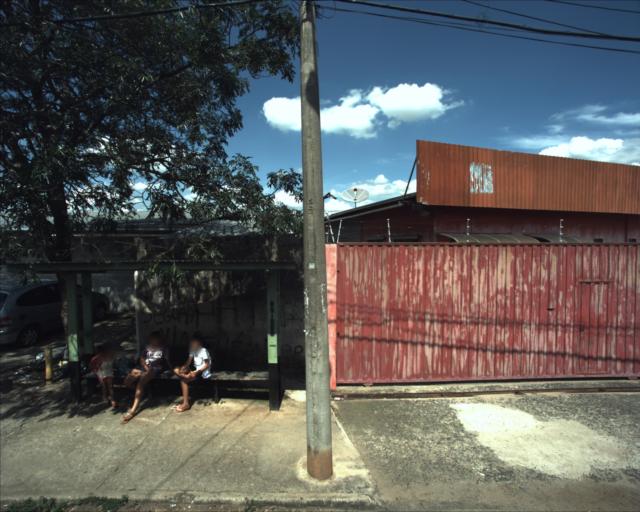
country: BR
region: Sao Paulo
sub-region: Sorocaba
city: Sorocaba
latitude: -23.4135
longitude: -47.4085
